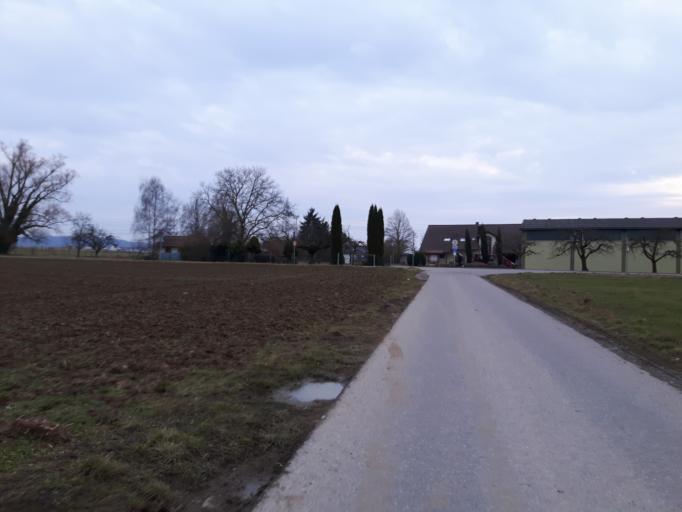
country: DE
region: Baden-Wuerttemberg
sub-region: Regierungsbezirk Stuttgart
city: Untereisesheim
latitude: 49.2192
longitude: 9.2297
